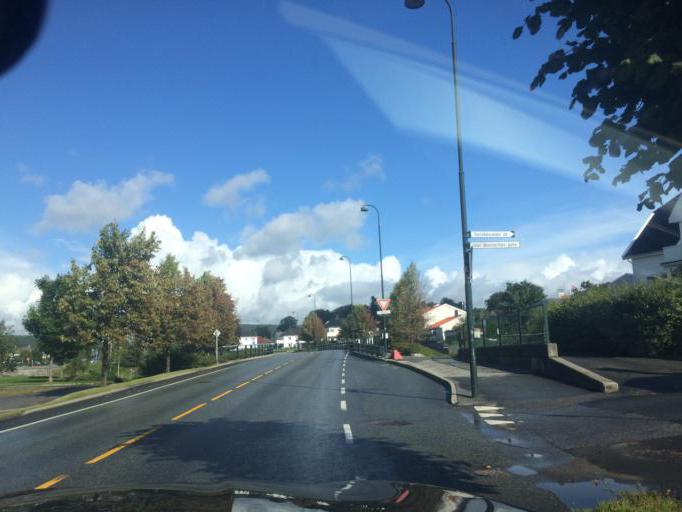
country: NO
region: Vest-Agder
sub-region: Kristiansand
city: Kristiansand
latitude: 58.1540
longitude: 8.0047
